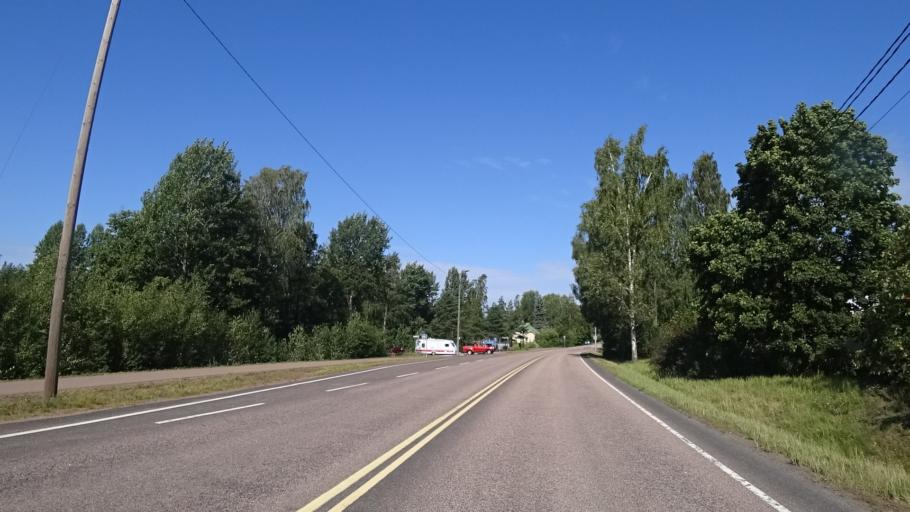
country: FI
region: Kymenlaakso
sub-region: Kotka-Hamina
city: Hamina
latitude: 60.5566
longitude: 27.2312
